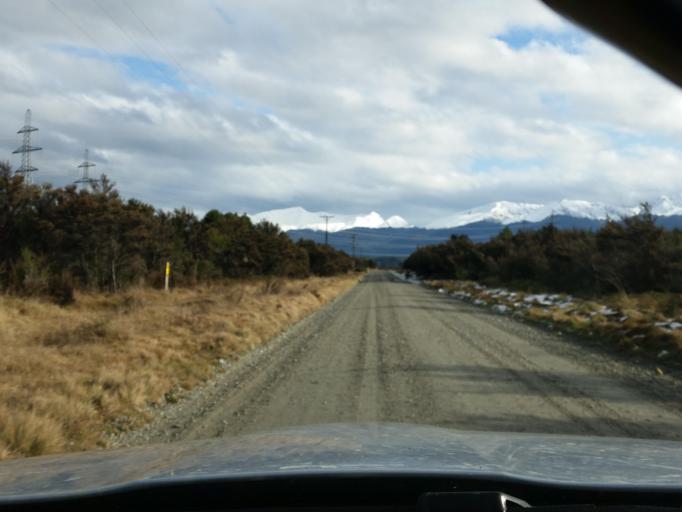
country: NZ
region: Southland
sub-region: Southland District
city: Te Anau
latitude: -45.7785
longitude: 167.5880
